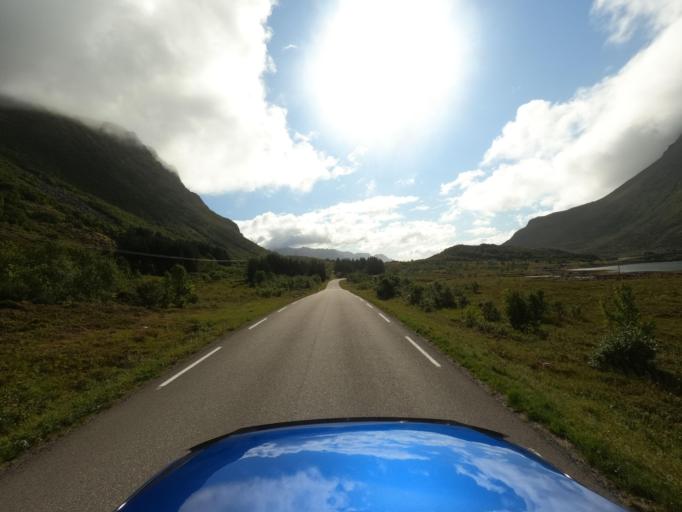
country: NO
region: Nordland
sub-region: Vagan
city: Kabelvag
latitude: 68.2738
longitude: 14.1656
